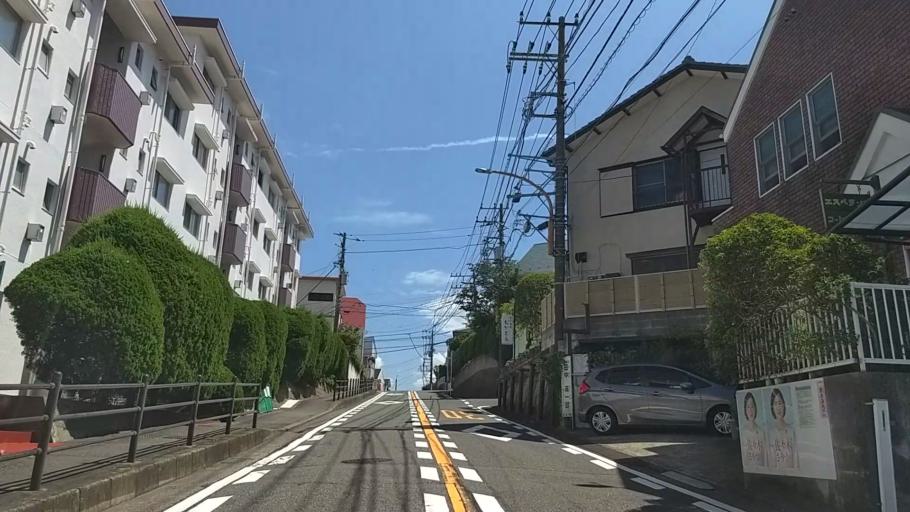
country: JP
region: Kanagawa
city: Zushi
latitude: 35.2916
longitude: 139.5913
